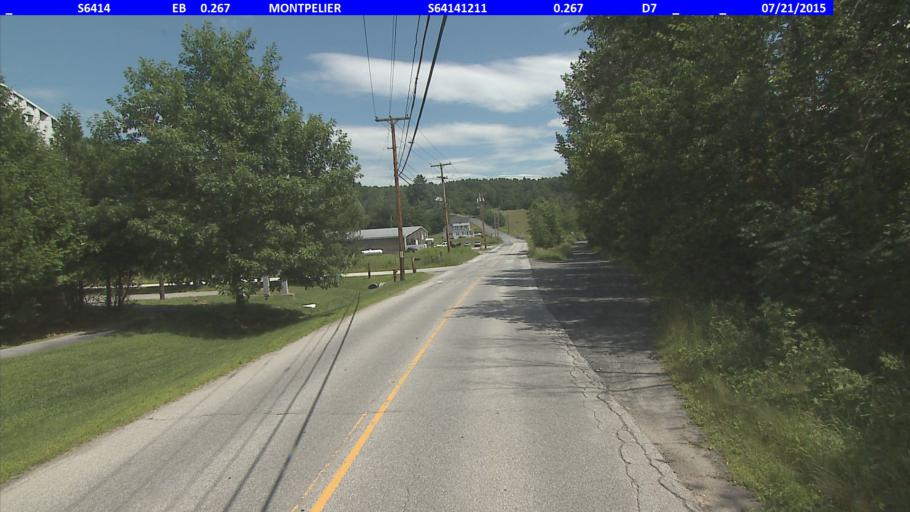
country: US
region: Vermont
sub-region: Washington County
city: Montpelier
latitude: 44.2427
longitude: -72.5395
